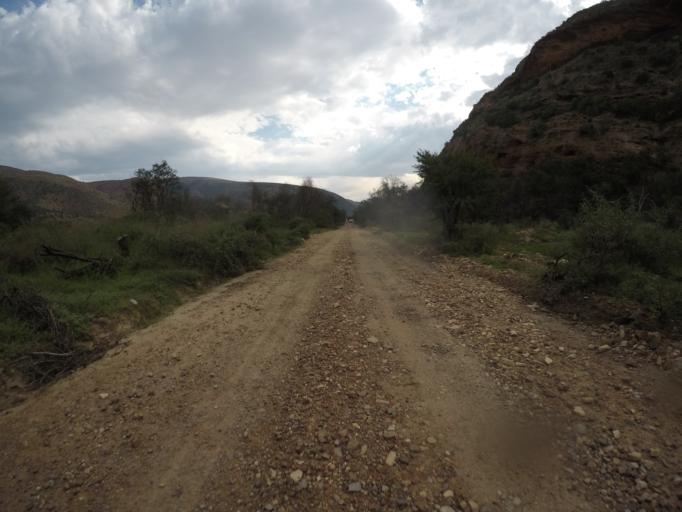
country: ZA
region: Eastern Cape
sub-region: Cacadu District Municipality
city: Kareedouw
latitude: -33.6038
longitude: 24.2029
